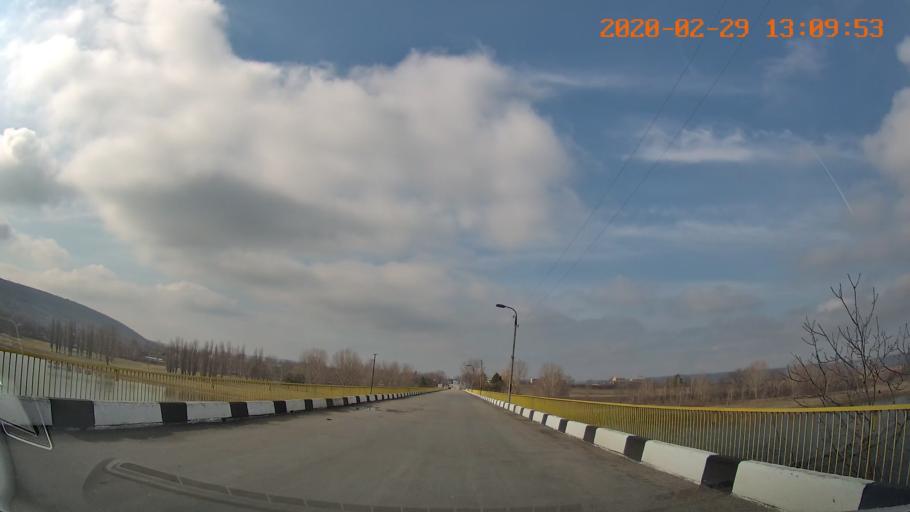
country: MD
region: Telenesti
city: Camenca
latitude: 48.0116
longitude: 28.7025
